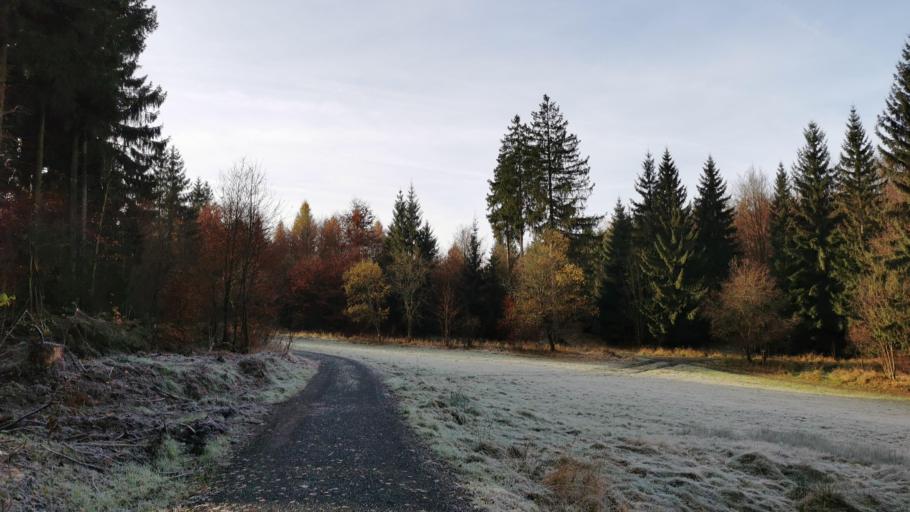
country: DE
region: Bavaria
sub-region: Upper Franconia
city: Ludwigsstadt
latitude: 50.4484
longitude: 11.3851
